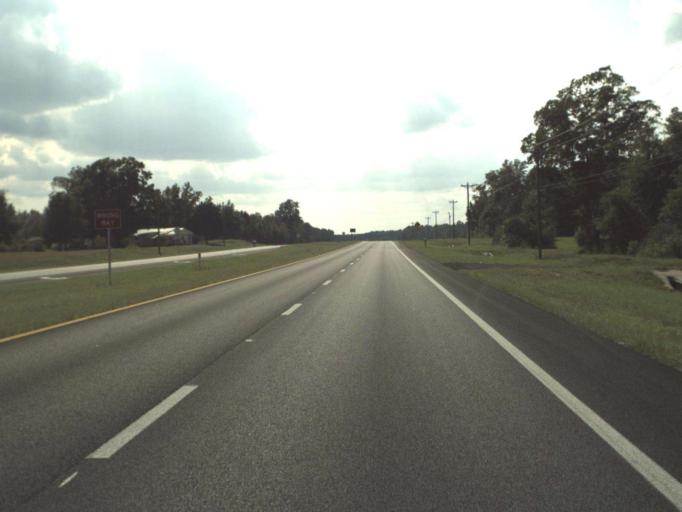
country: US
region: Florida
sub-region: Bay County
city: Laguna Beach
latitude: 30.4698
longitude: -85.8535
